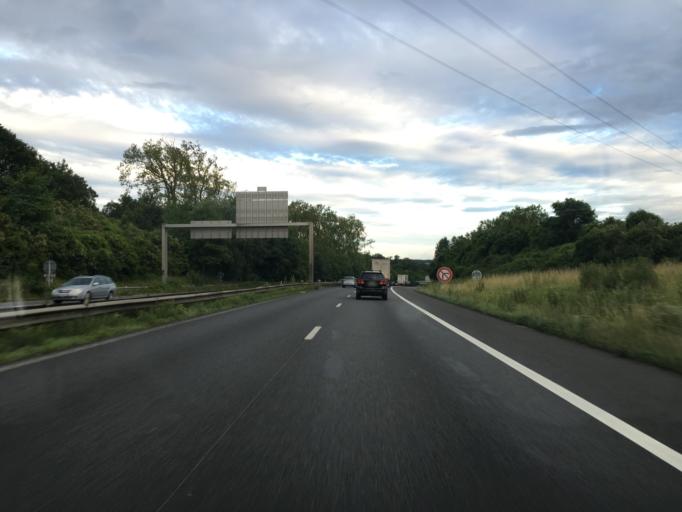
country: FR
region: Ile-de-France
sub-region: Departement de Seine-et-Marne
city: Brie-Comte-Robert
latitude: 48.6770
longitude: 2.6095
